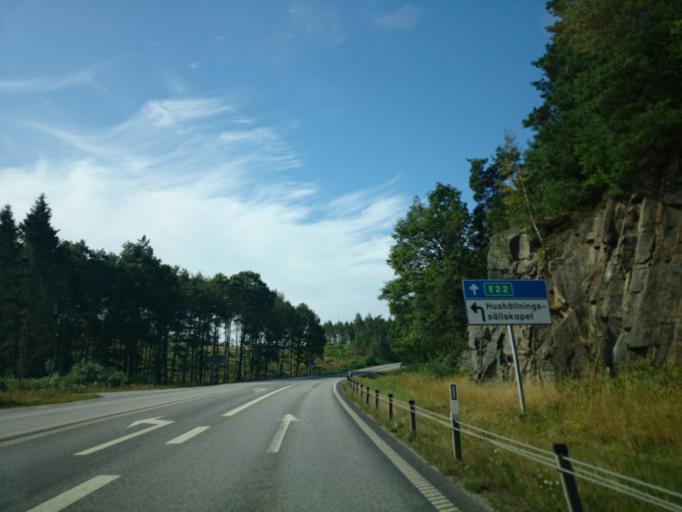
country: SE
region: Kalmar
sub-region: Vasterviks Kommun
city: Gamleby
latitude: 57.9164
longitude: 16.3995
